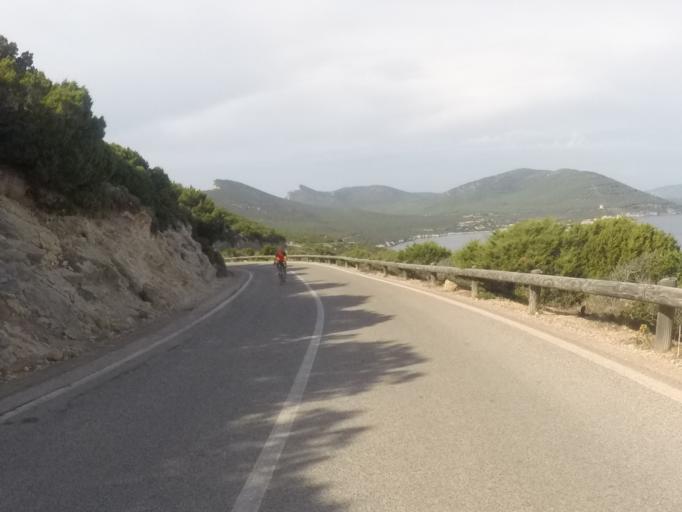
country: IT
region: Sardinia
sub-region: Provincia di Sassari
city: Alghero
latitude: 40.5656
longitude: 8.1645
